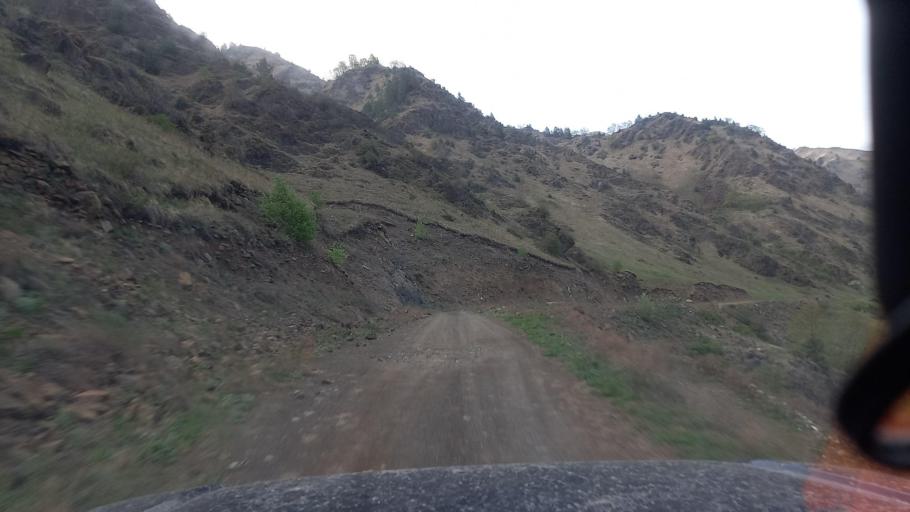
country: RU
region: Kabardino-Balkariya
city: Kamennomostskoye
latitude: 43.7214
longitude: 42.8450
